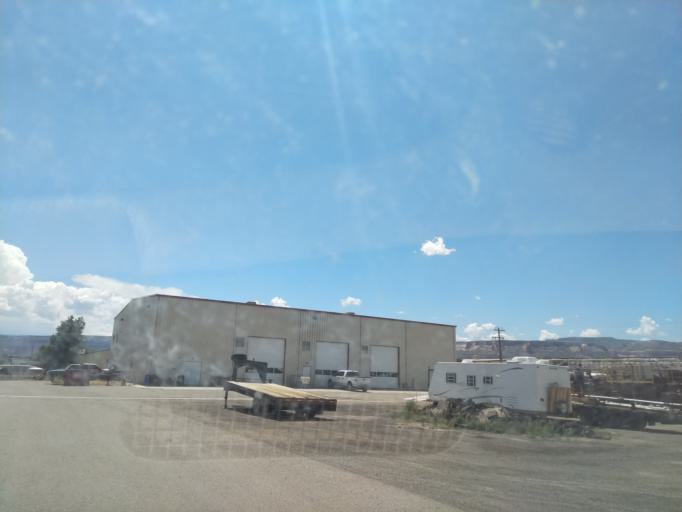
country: US
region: Colorado
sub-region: Mesa County
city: Redlands
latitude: 39.1185
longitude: -108.6561
